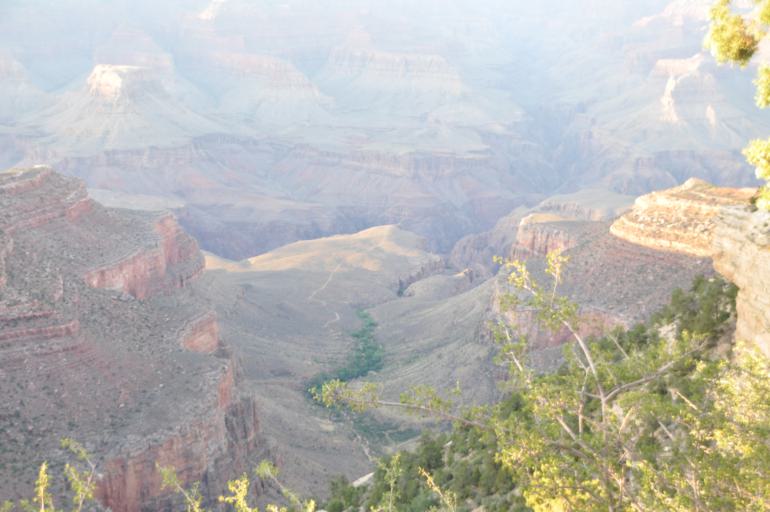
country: US
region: Arizona
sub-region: Coconino County
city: Grand Canyon
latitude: 36.0569
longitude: -112.1400
